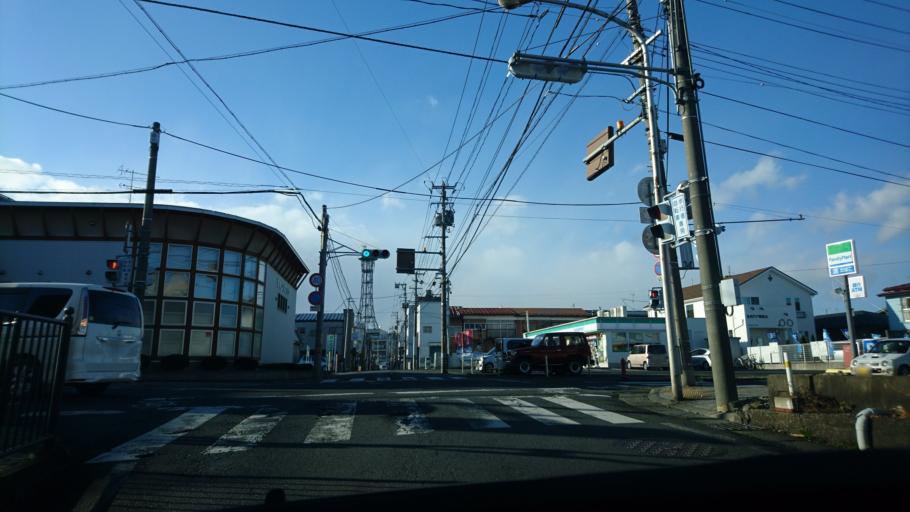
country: JP
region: Iwate
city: Mizusawa
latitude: 39.1415
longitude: 141.1459
